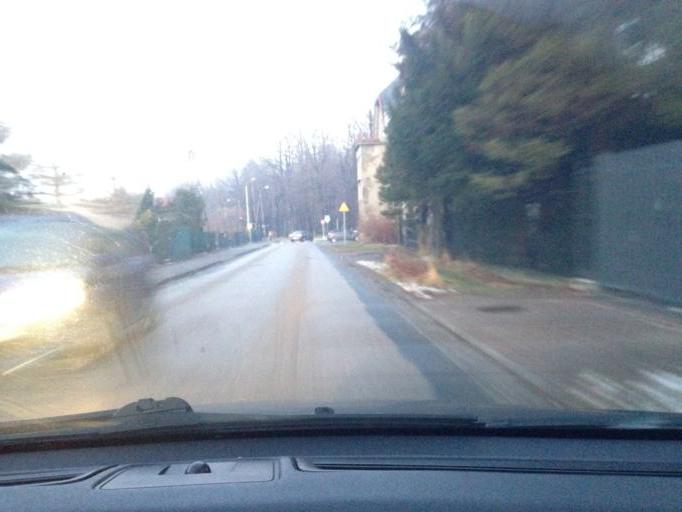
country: PL
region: Silesian Voivodeship
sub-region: Powiat bielski
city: Bystra
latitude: 49.7884
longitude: 19.0456
